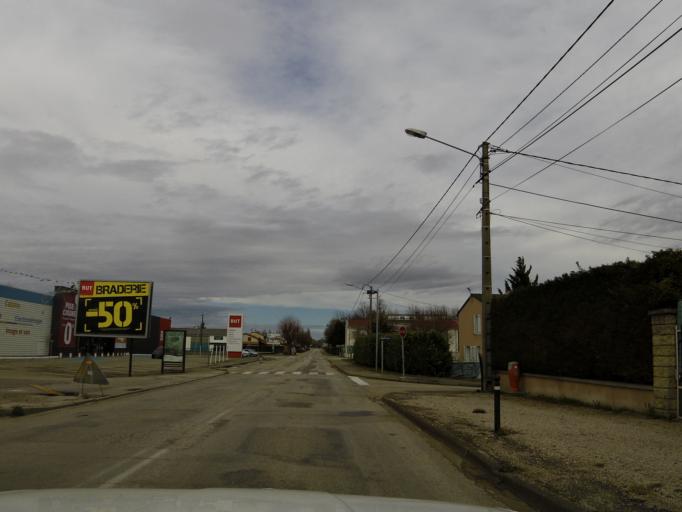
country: FR
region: Rhone-Alpes
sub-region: Departement de l'Ain
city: Amberieu-en-Bugey
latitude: 45.9600
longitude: 5.3347
